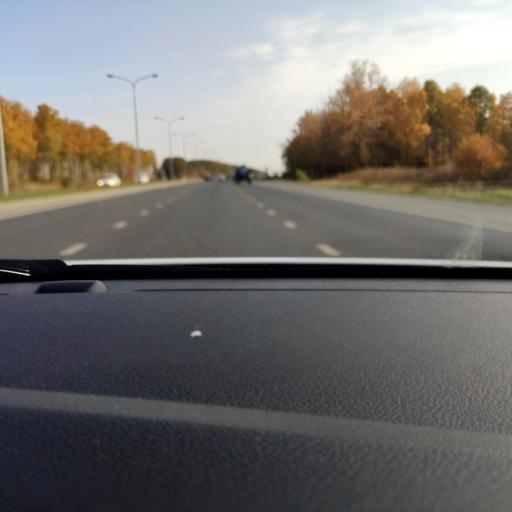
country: RU
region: Tatarstan
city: Vysokaya Gora
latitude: 55.8010
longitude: 49.3164
